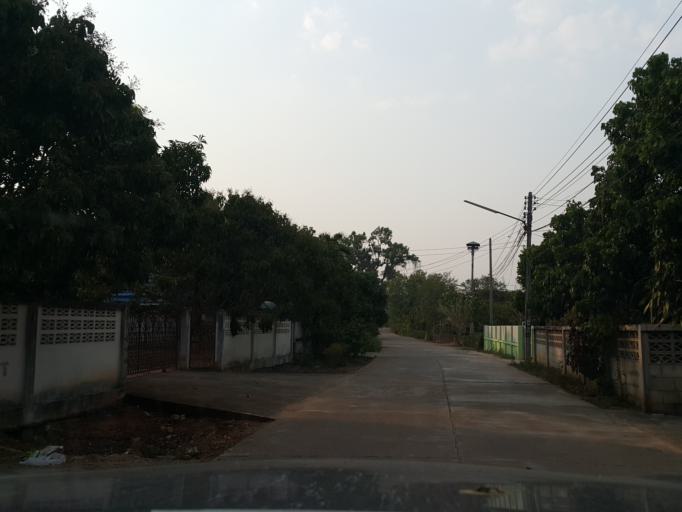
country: TH
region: Lamphun
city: Li
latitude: 17.8058
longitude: 98.9505
